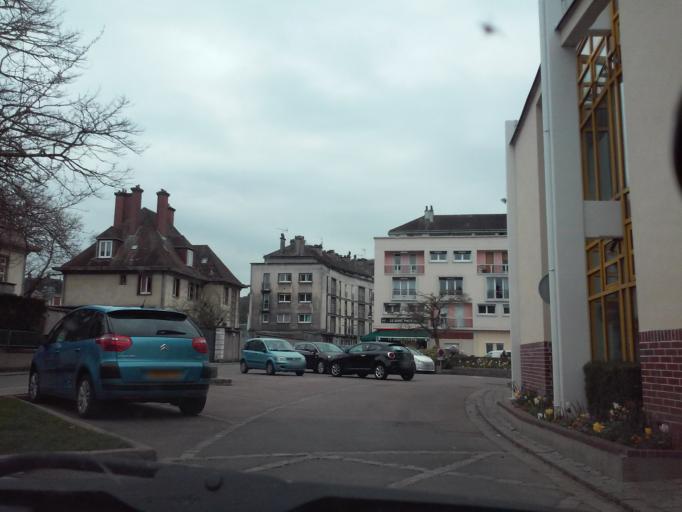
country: FR
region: Haute-Normandie
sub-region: Departement de la Seine-Maritime
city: Caudebec-en-Caux
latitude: 49.5249
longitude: 0.7250
